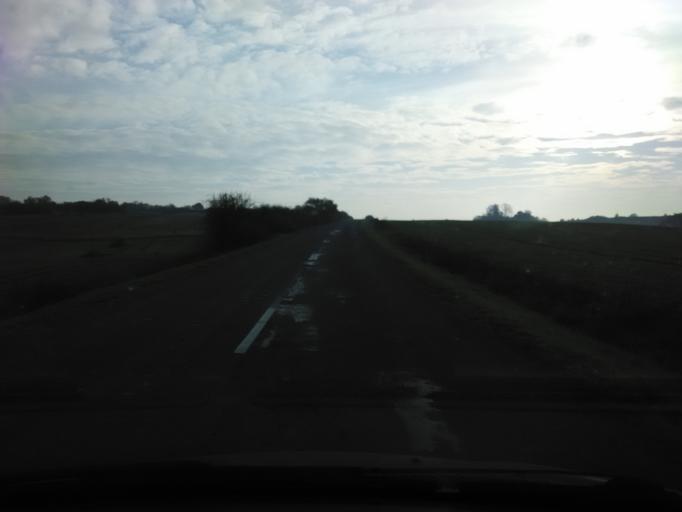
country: SK
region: Nitriansky
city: Levice
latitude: 48.2891
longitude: 18.6740
